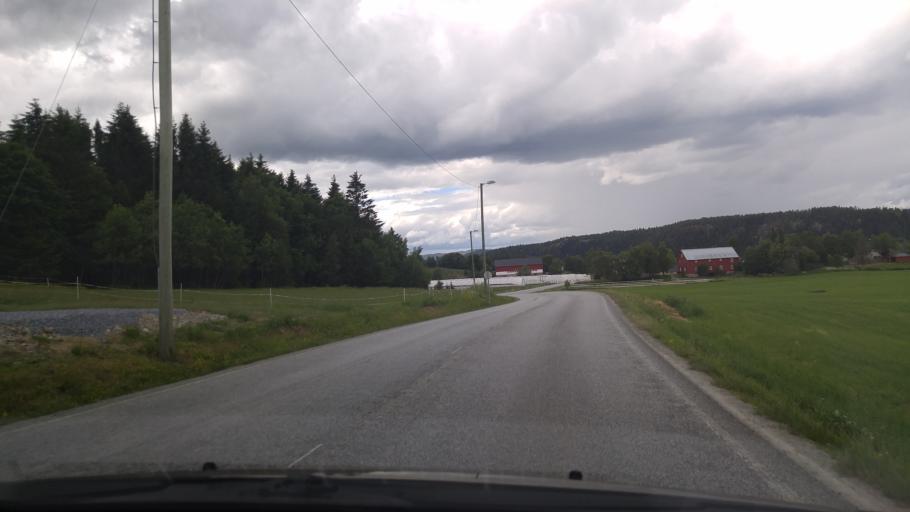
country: NO
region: Nord-Trondelag
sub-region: Steinkjer
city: Steinkjer
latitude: 64.0967
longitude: 11.4428
